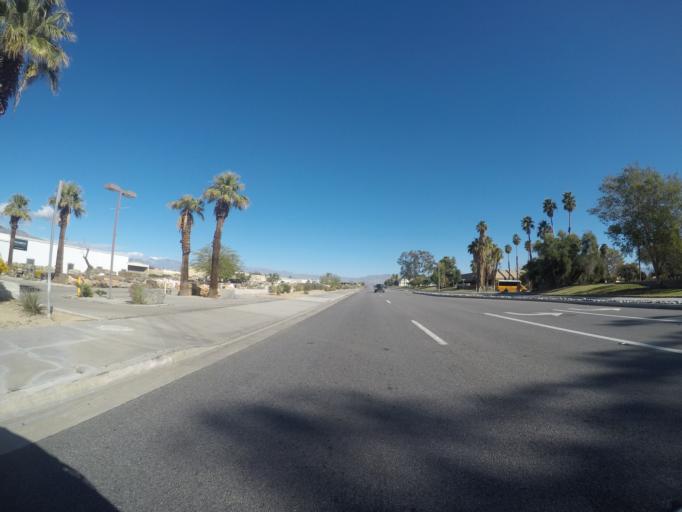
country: US
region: California
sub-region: Riverside County
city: Cathedral City
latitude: 33.8095
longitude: -116.4930
